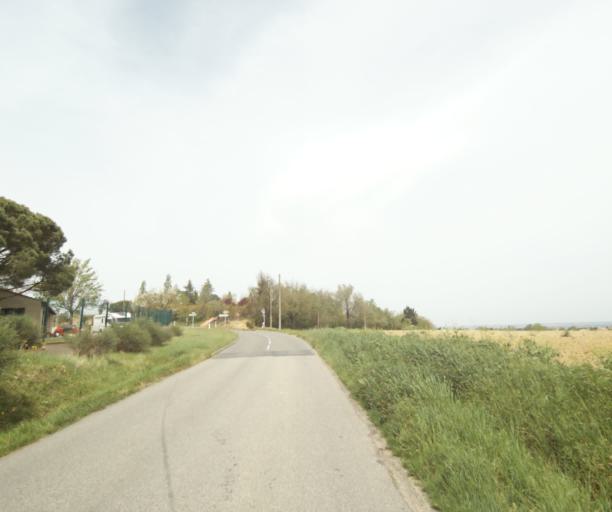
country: FR
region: Midi-Pyrenees
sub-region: Departement de la Haute-Garonne
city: Pompertuzat
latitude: 43.4887
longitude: 1.4998
